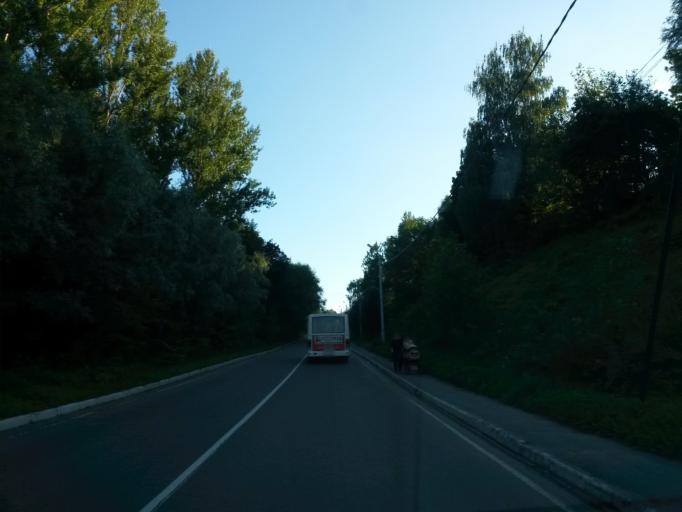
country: RU
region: Jaroslavl
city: Tutayev
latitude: 57.8713
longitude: 39.5376
